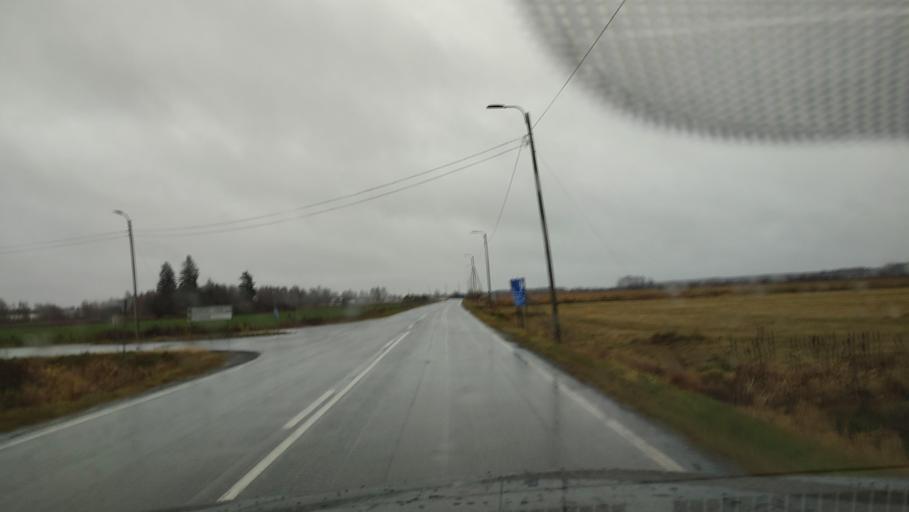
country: FI
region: Ostrobothnia
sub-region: Vaasa
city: Ristinummi
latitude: 63.0462
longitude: 21.7449
